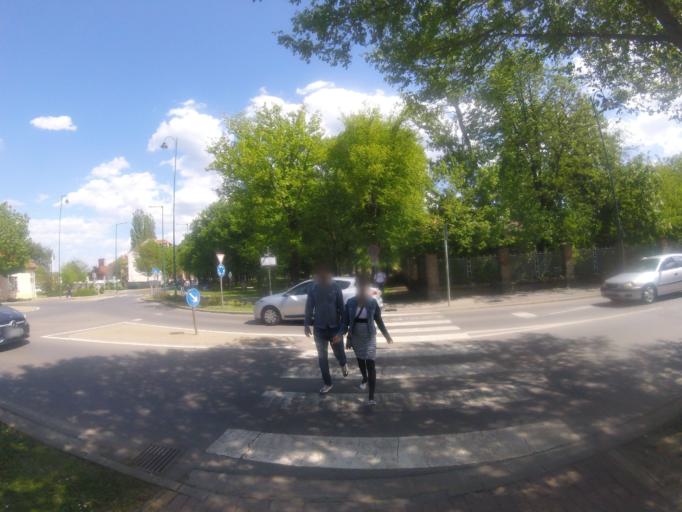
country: HU
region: Bekes
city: Gyula
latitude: 46.6447
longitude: 21.2805
